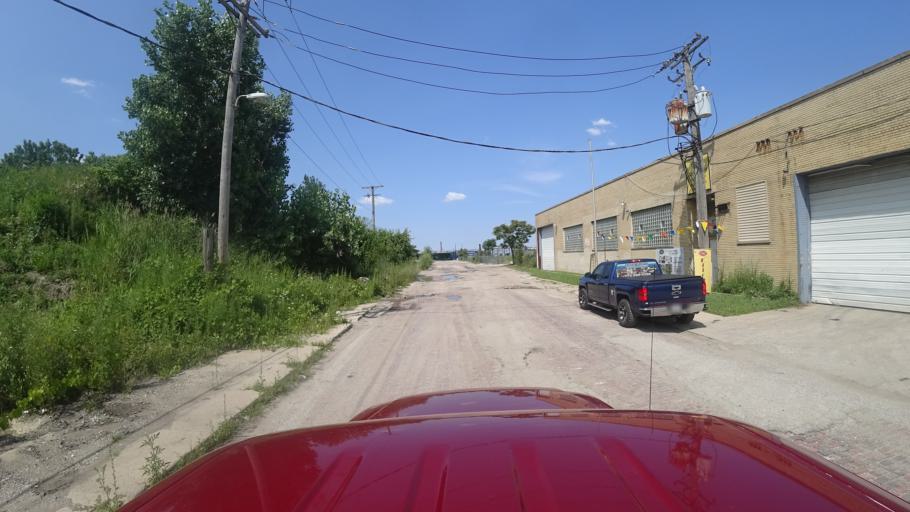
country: US
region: Illinois
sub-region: Cook County
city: Cicero
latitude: 41.8052
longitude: -87.7009
